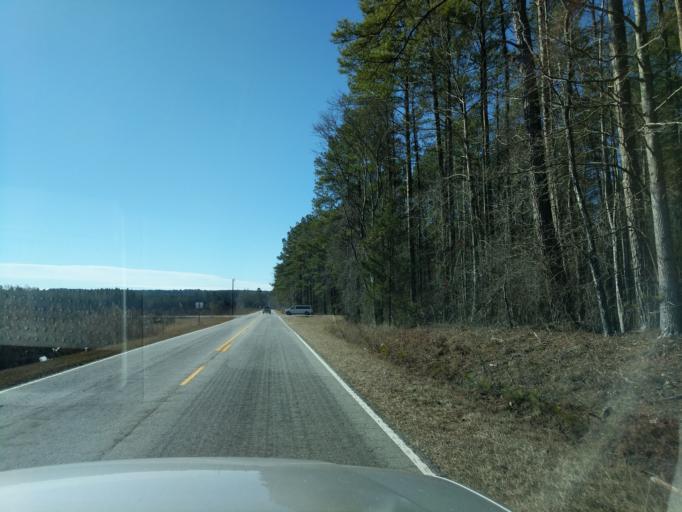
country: US
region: South Carolina
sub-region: Laurens County
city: Joanna
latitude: 34.2646
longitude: -81.8562
